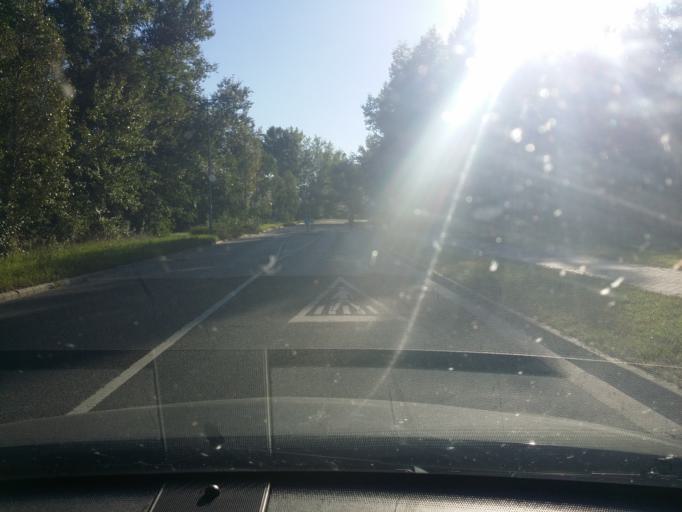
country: HU
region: Budapest
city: Budapest XV. keruelet
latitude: 47.5994
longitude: 19.1124
